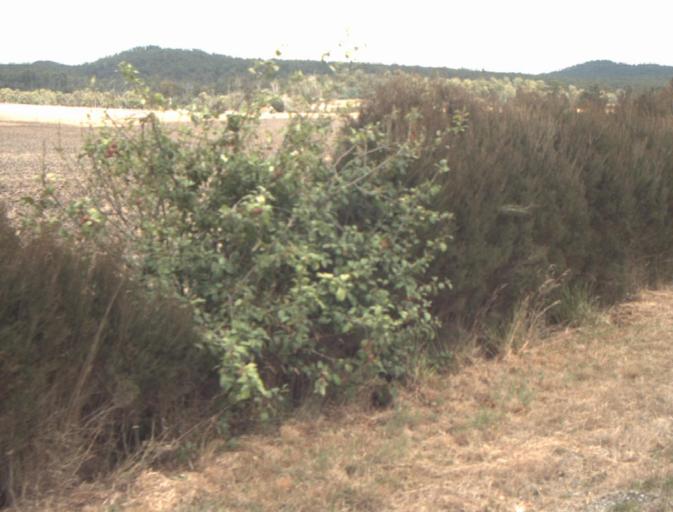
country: AU
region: Tasmania
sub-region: Launceston
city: Mayfield
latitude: -41.2066
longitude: 147.0616
